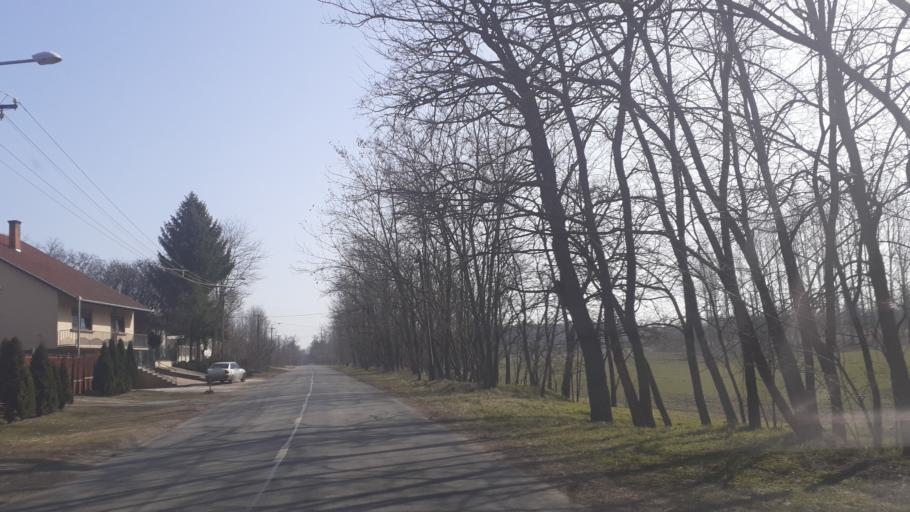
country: HU
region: Pest
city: Orkeny
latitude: 47.0755
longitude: 19.3749
